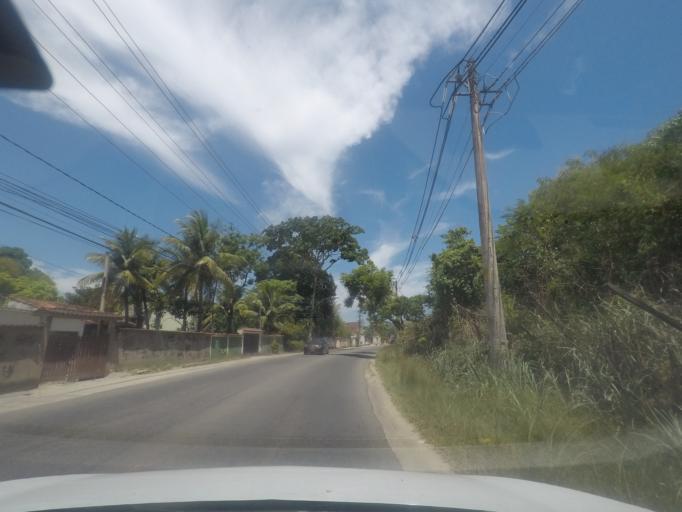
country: BR
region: Rio de Janeiro
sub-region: Itaguai
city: Itaguai
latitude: -22.9853
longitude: -43.6563
